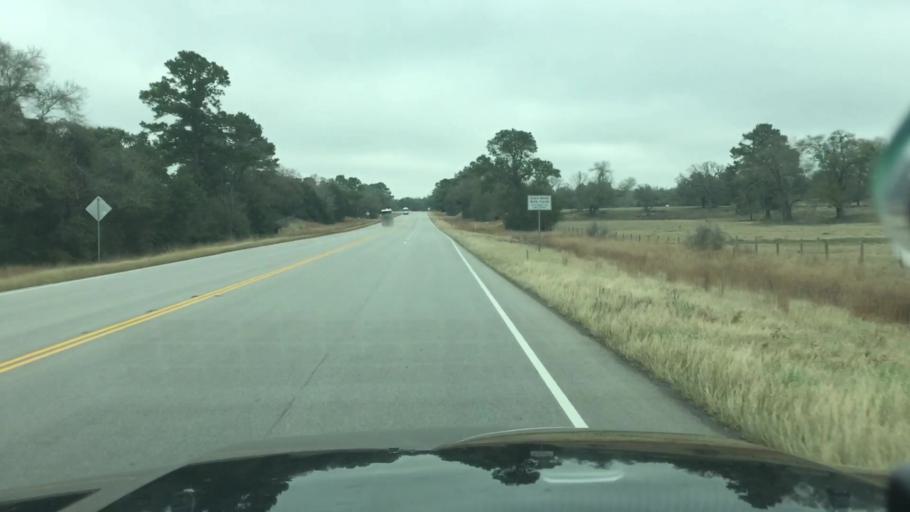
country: US
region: Texas
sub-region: Lee County
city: Giddings
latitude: 30.0871
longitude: -96.9152
